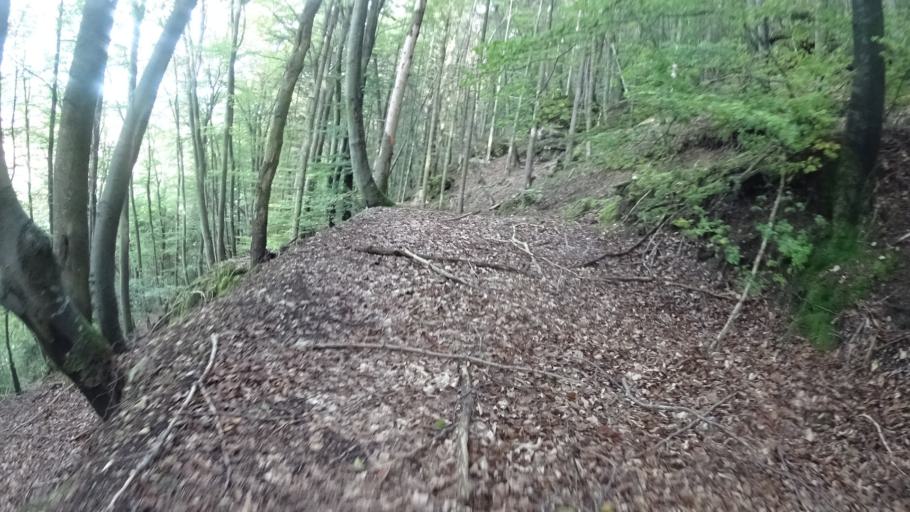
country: DE
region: Bavaria
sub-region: Upper Bavaria
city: Walting
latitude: 48.9053
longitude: 11.3017
